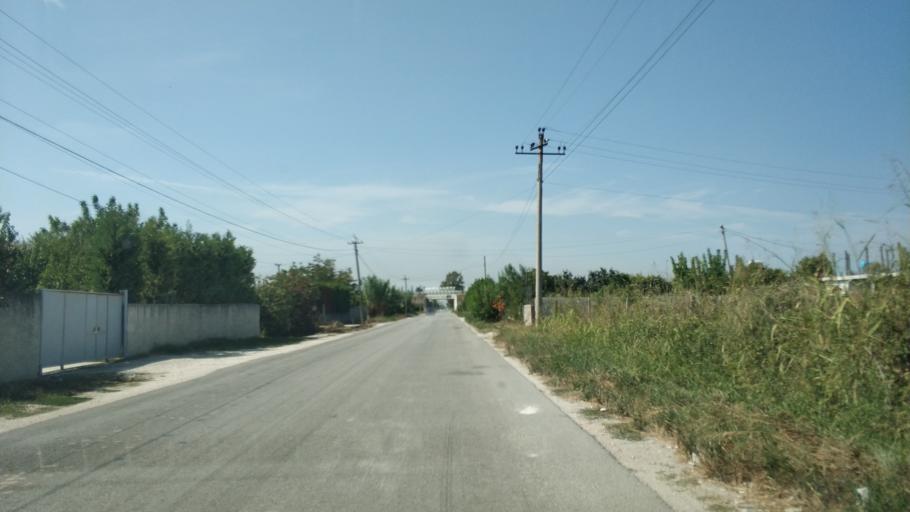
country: AL
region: Fier
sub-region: Rrethi i Fierit
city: Dermenas
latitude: 40.7419
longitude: 19.5043
